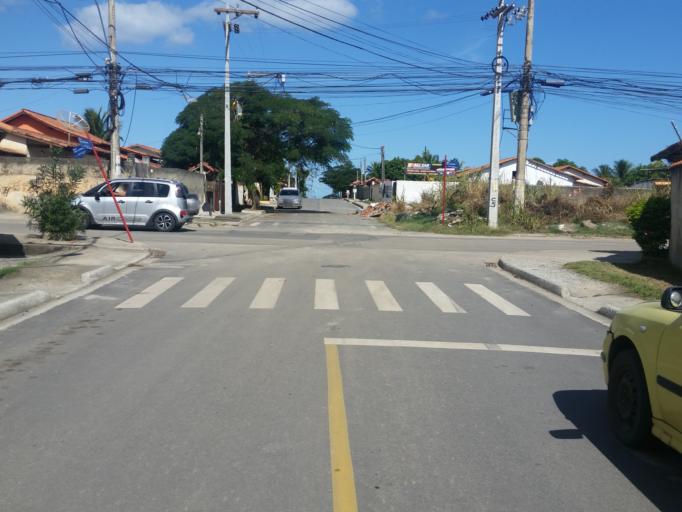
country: BR
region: Rio de Janeiro
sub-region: Marica
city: Marica
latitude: -22.9645
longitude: -42.9667
